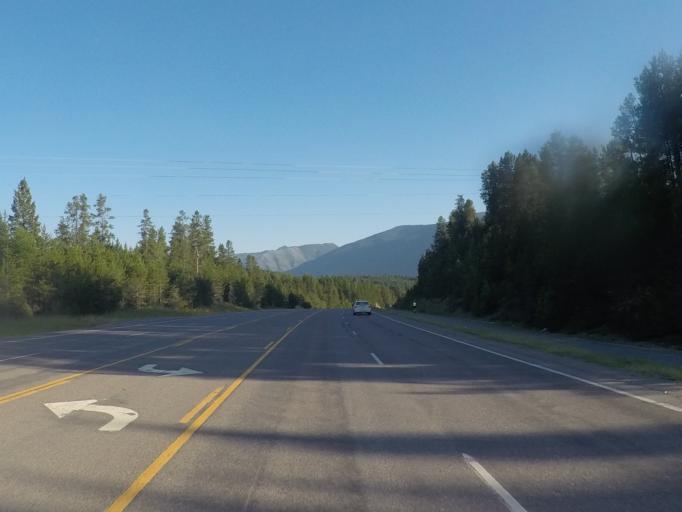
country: US
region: Montana
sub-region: Flathead County
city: Columbia Falls
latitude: 48.4284
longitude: -114.0424
